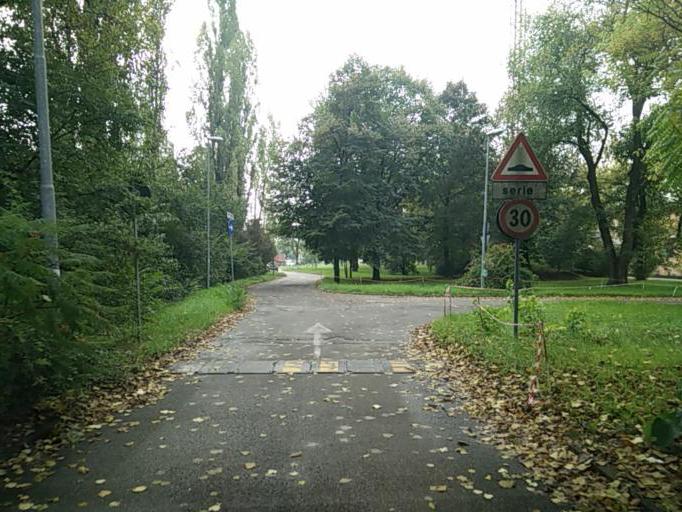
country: IT
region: Emilia-Romagna
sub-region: Provincia di Modena
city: Carpi Centro
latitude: 44.7826
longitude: 10.8676
